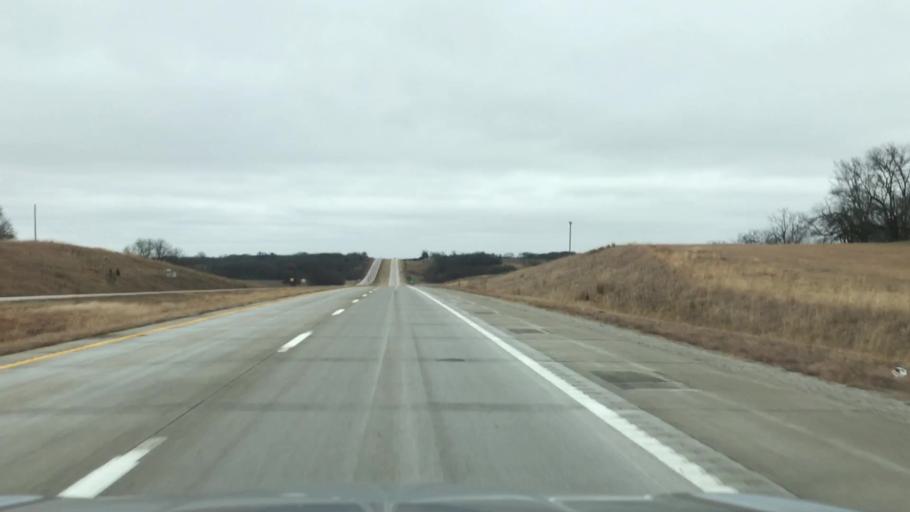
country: US
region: Missouri
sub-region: Livingston County
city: Chillicothe
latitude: 39.7350
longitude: -93.7631
